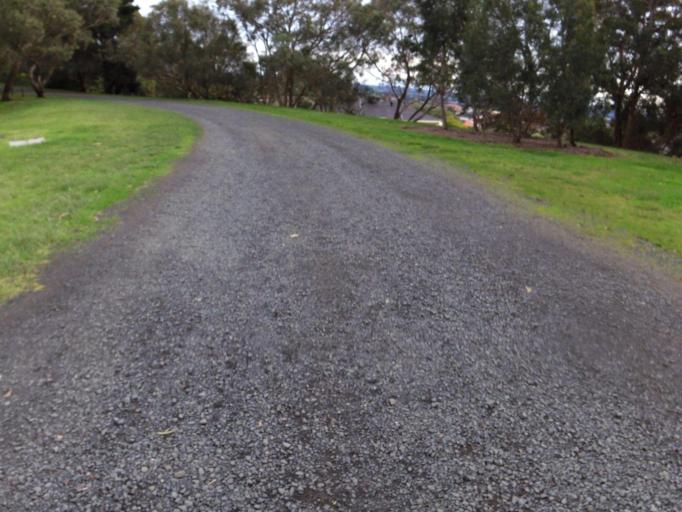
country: AU
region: Victoria
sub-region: Casey
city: Berwick
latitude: -38.0228
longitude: 145.3415
